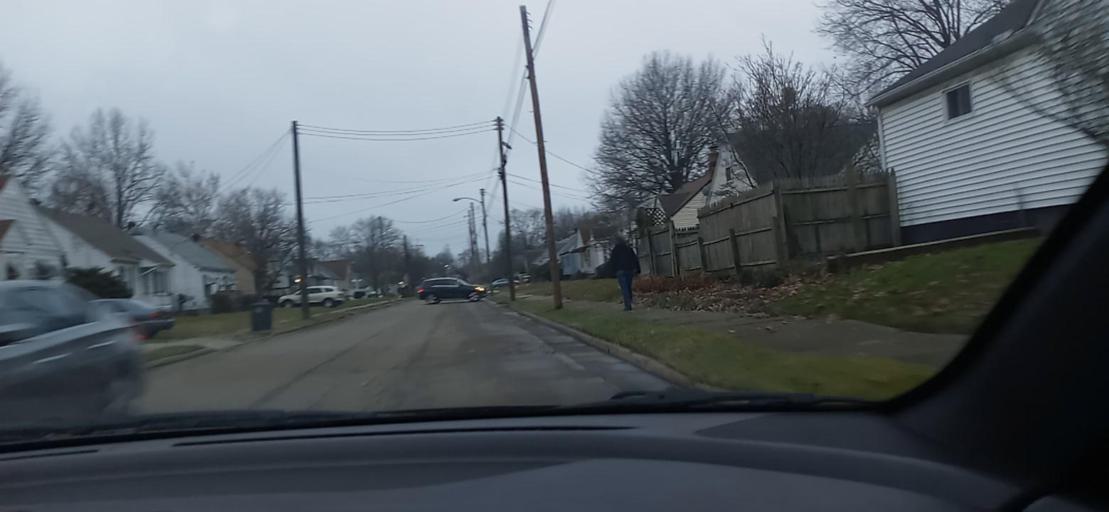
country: US
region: Ohio
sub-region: Summit County
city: Akron
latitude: 41.0444
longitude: -81.5030
